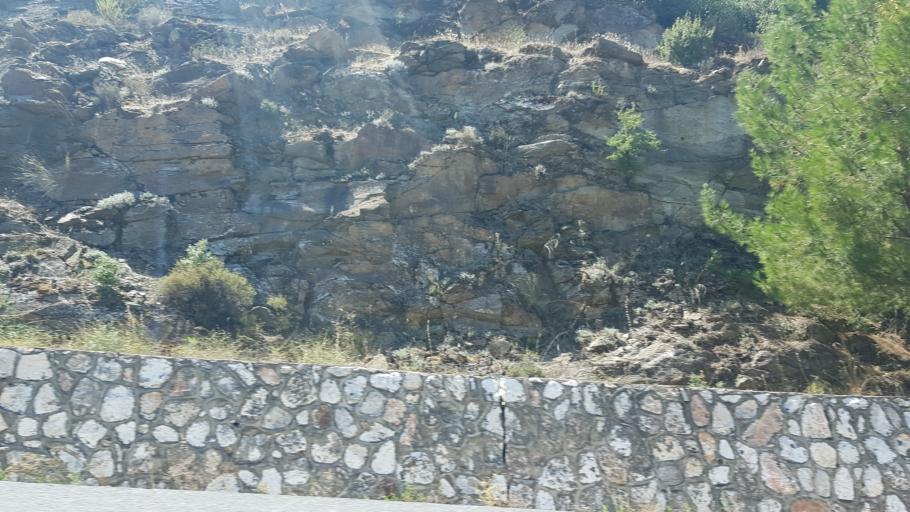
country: TR
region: Aydin
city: Akcaova
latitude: 37.5030
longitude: 28.1038
